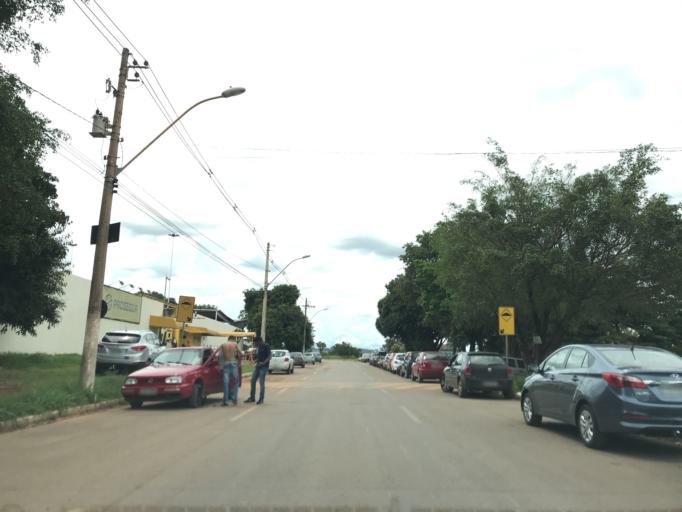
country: BR
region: Federal District
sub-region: Brasilia
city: Brasilia
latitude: -15.7889
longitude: -47.9867
